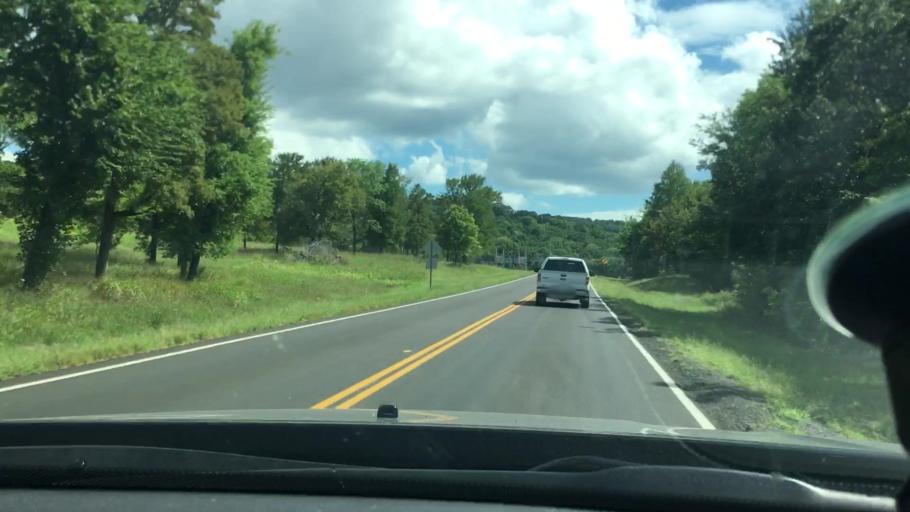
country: US
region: Oklahoma
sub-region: Sequoyah County
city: Vian
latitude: 35.6427
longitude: -94.9610
